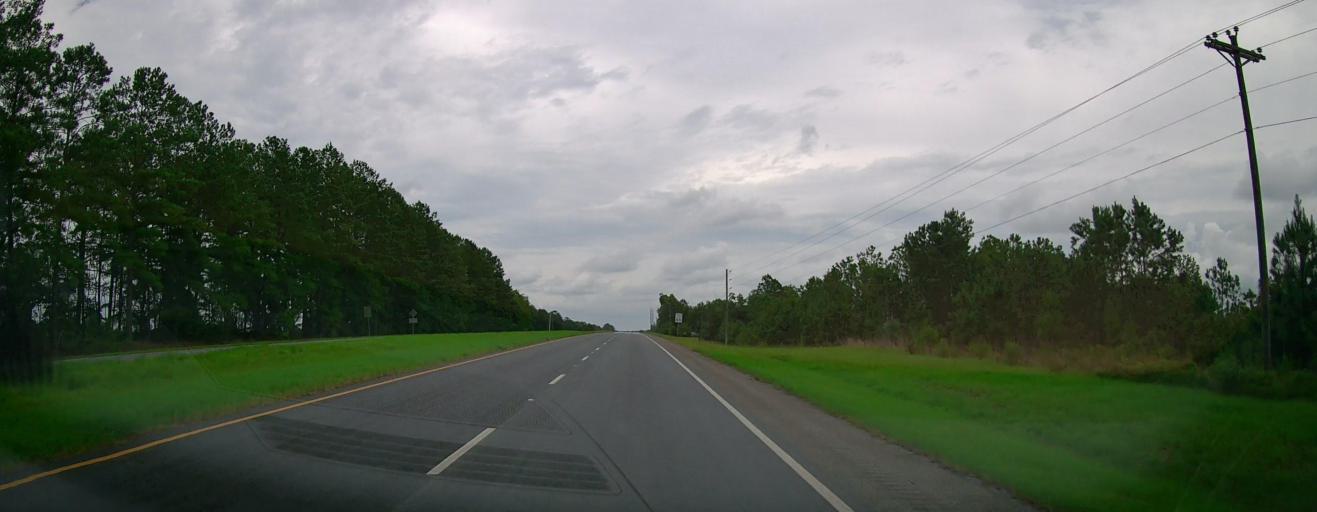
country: US
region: Georgia
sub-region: Dodge County
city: Eastman
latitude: 32.1201
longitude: -83.1125
